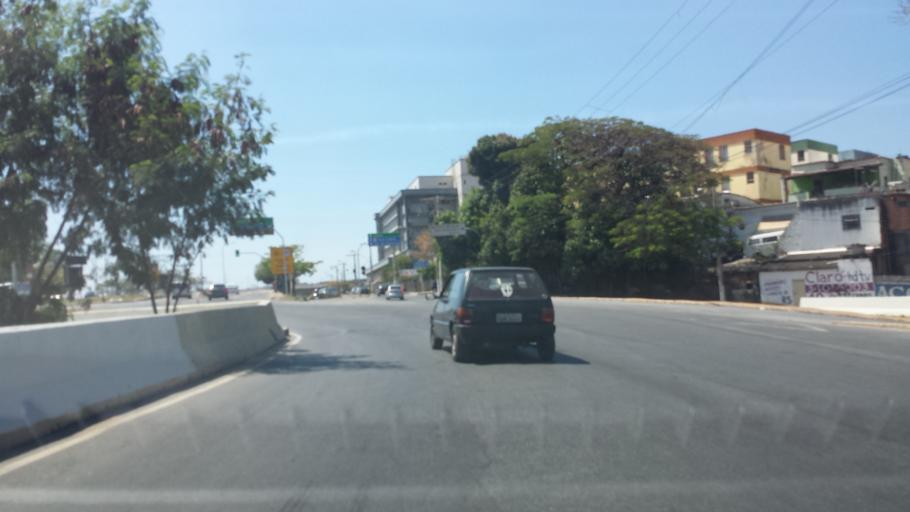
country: BR
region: Minas Gerais
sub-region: Belo Horizonte
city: Belo Horizonte
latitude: -19.8190
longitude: -43.9505
